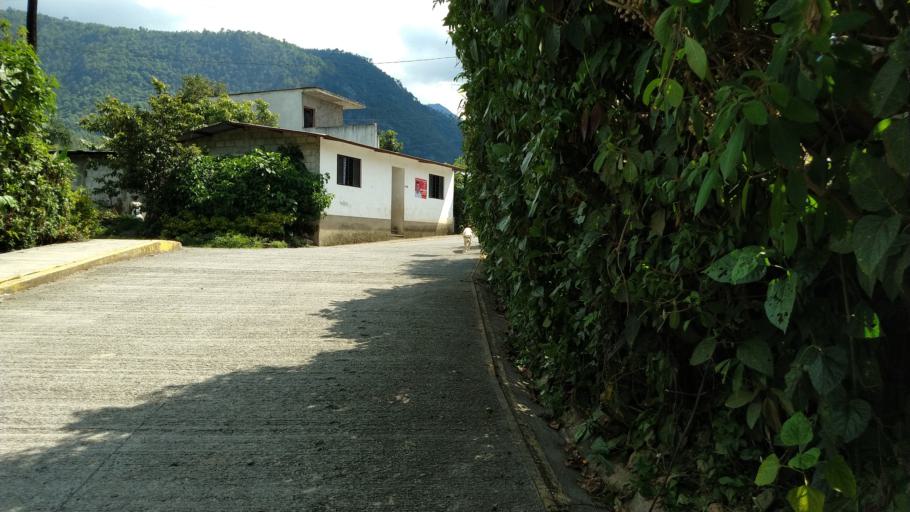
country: MX
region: Veracruz
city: Jalapilla
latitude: 18.8110
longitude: -97.0698
